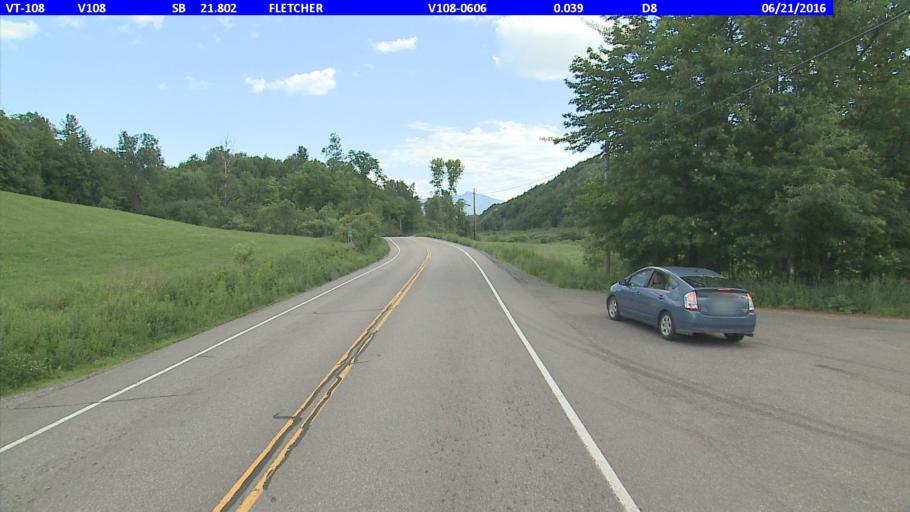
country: US
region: Vermont
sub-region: Lamoille County
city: Johnson
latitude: 44.7047
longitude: -72.8309
